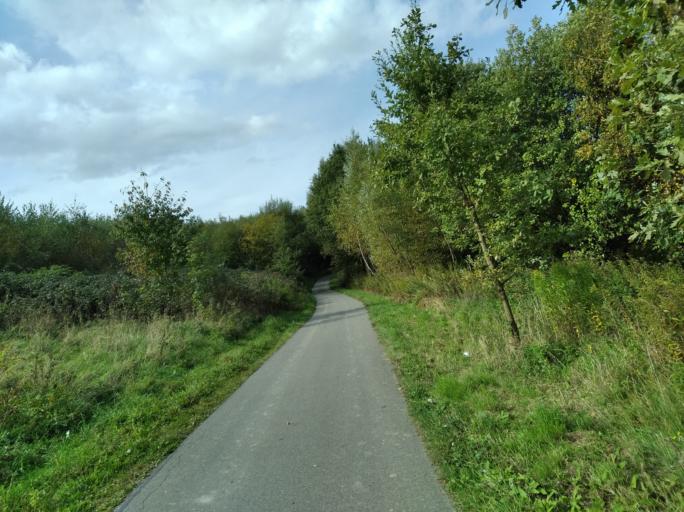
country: PL
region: Subcarpathian Voivodeship
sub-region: Powiat strzyzowski
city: Jawornik
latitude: 49.8377
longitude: 21.8838
